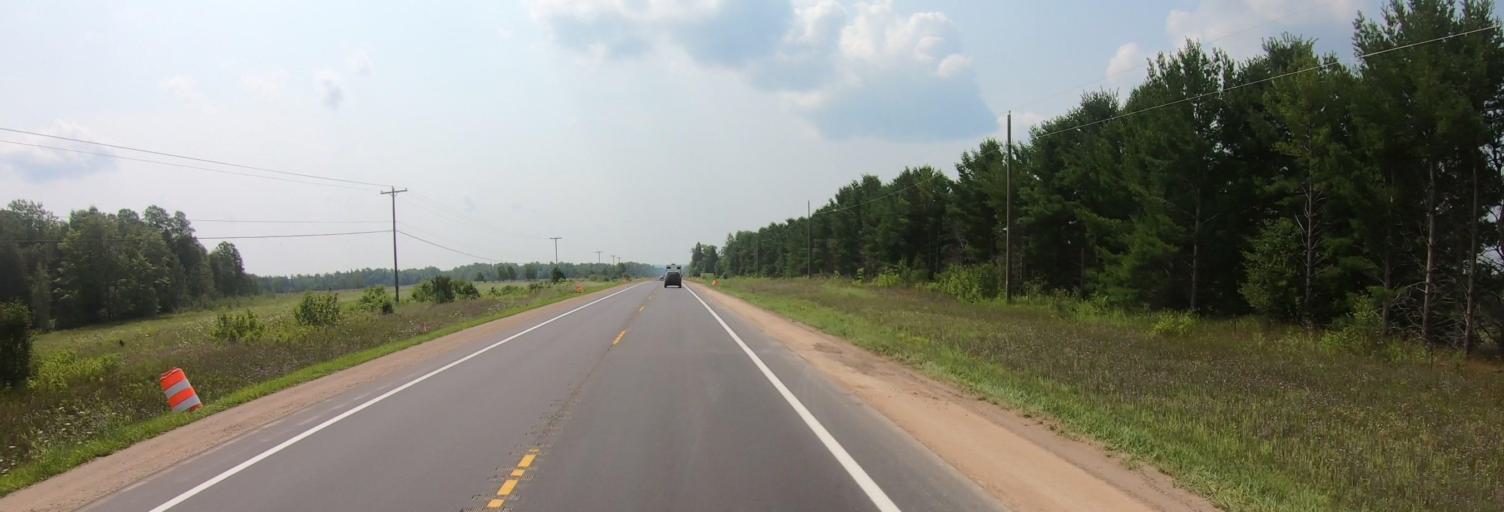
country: US
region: Michigan
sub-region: Luce County
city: Newberry
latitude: 46.4035
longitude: -85.5100
